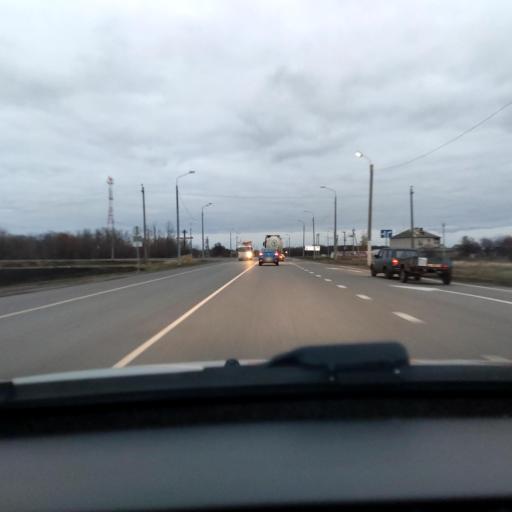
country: RU
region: Lipetsk
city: Borinskoye
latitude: 52.4617
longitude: 39.3274
